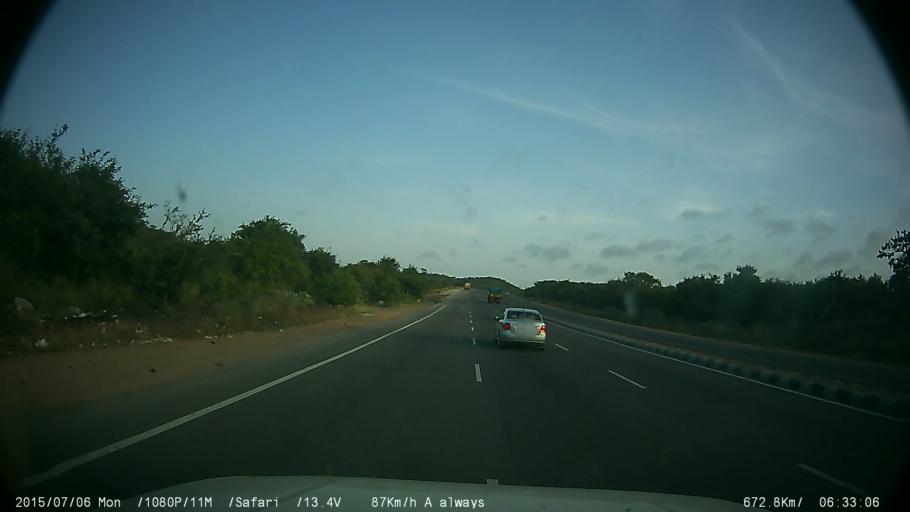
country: IN
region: Tamil Nadu
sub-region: Krishnagiri
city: Hosur
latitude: 12.6908
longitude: 77.9198
